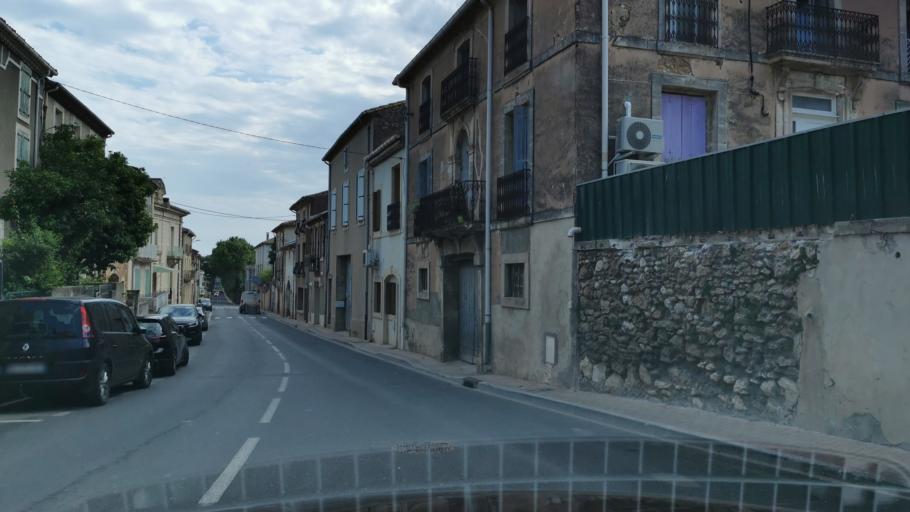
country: FR
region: Languedoc-Roussillon
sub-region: Departement de l'Herault
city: Puisserguier
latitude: 43.3667
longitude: 3.0403
